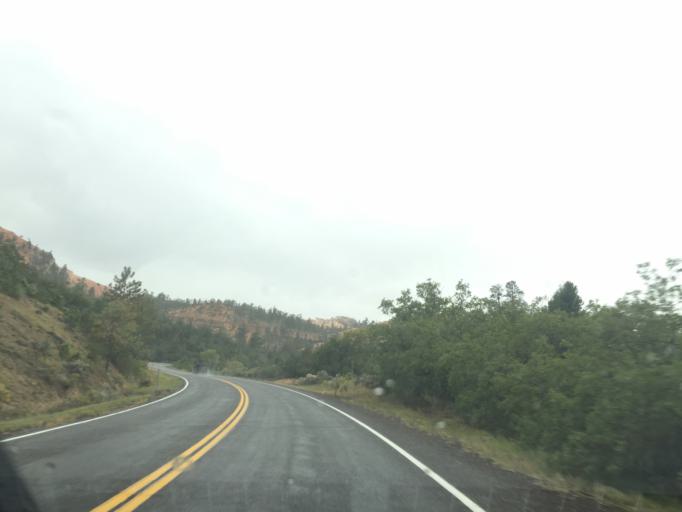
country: US
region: Utah
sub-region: Garfield County
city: Panguitch
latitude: 37.6631
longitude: -112.1018
